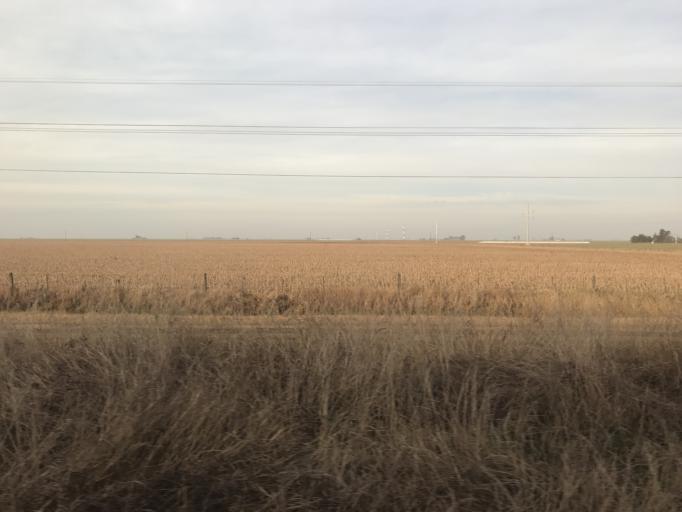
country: AR
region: Cordoba
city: Marcos Juarez
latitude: -32.6846
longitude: -62.1865
